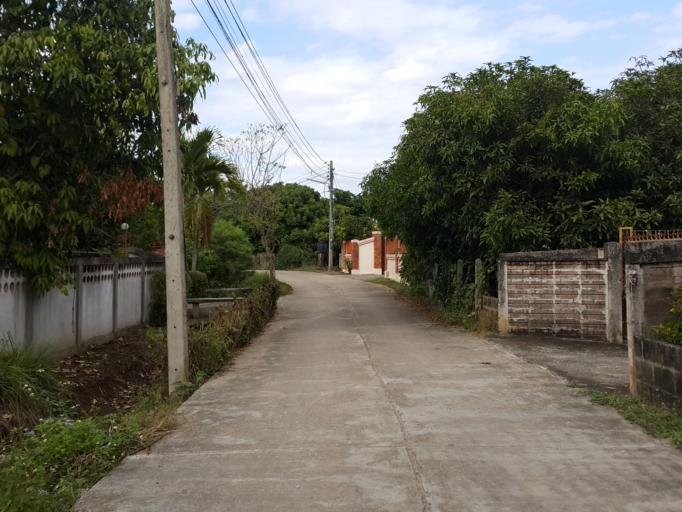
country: TH
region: Chiang Mai
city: San Sai
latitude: 18.8737
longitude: 99.1007
